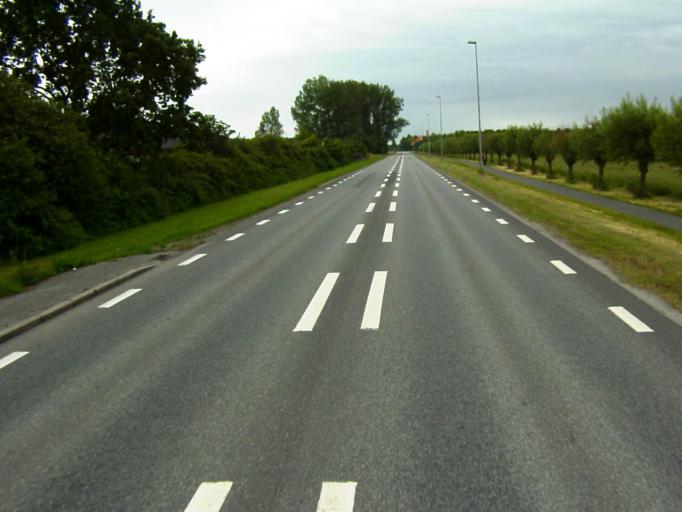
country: SE
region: Skane
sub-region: Kristianstads Kommun
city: Kristianstad
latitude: 56.0076
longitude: 14.1518
